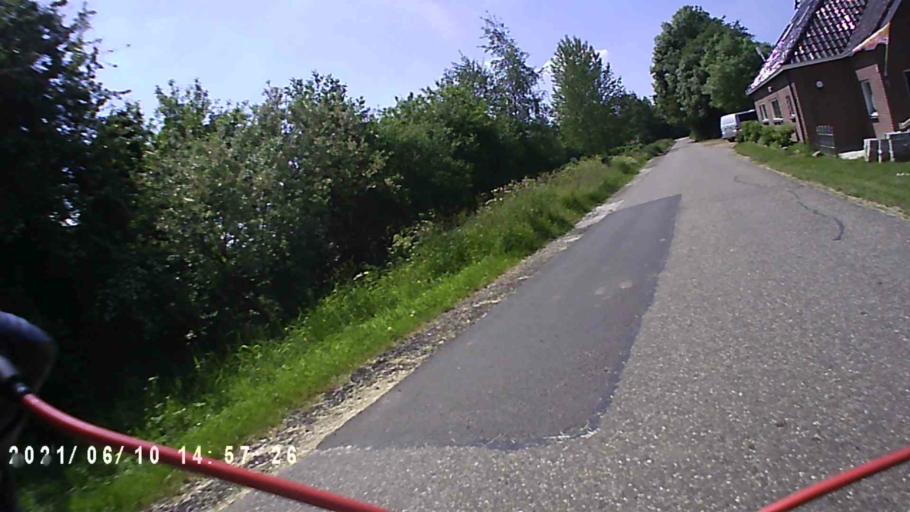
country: NL
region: Groningen
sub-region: Gemeente Grootegast
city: Grootegast
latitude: 53.2165
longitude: 6.2415
